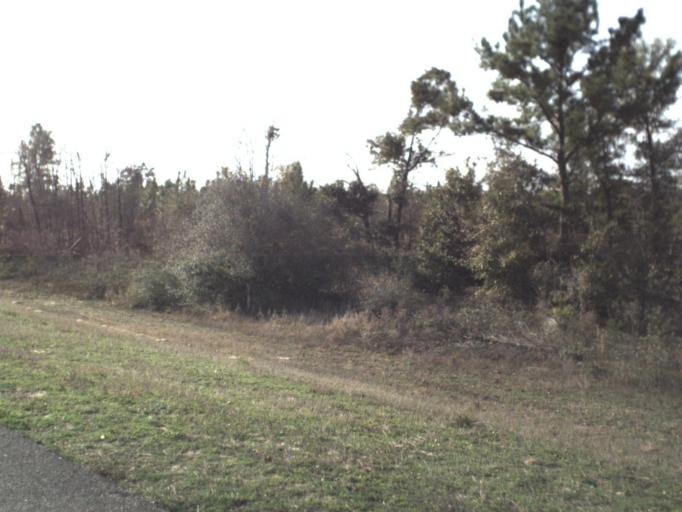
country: US
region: Florida
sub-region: Bay County
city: Youngstown
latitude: 30.4345
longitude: -85.5313
